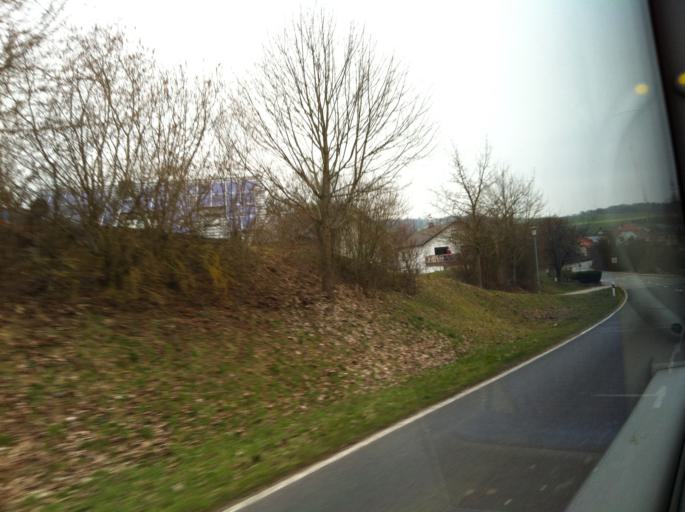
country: DE
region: Baden-Wuerttemberg
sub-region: Karlsruhe Region
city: Fahrenbach
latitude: 49.4500
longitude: 9.1620
